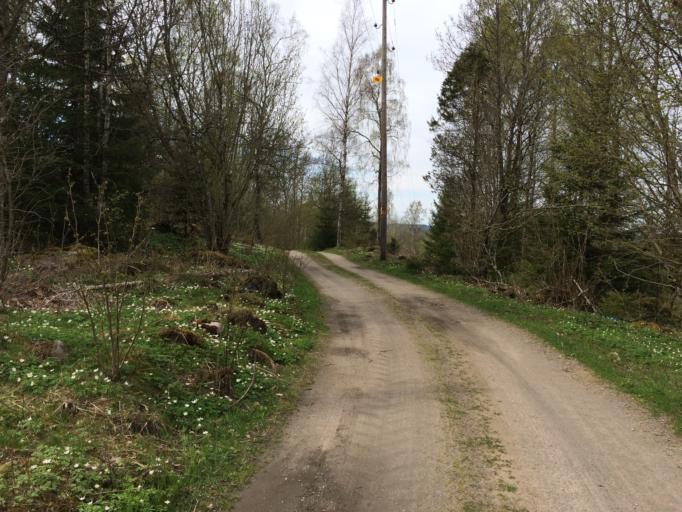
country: SE
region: Vaestra Goetaland
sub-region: Ulricehamns Kommun
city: Ulricehamn
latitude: 57.7278
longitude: 13.4343
